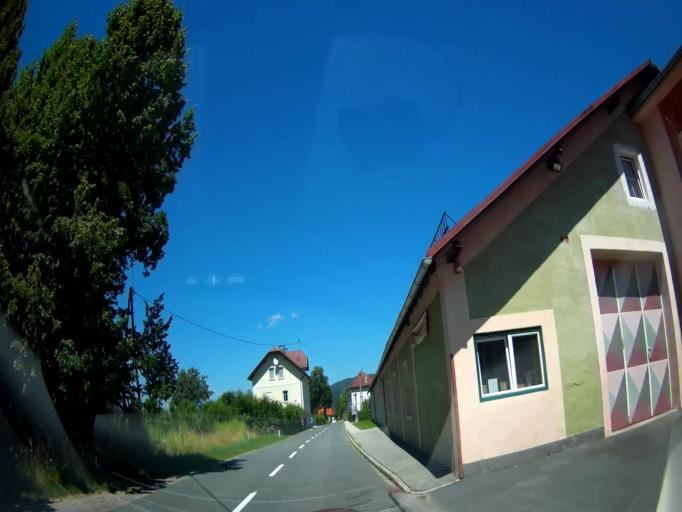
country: AT
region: Carinthia
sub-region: Politischer Bezirk Klagenfurt Land
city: Ferlach
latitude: 46.5174
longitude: 14.2965
